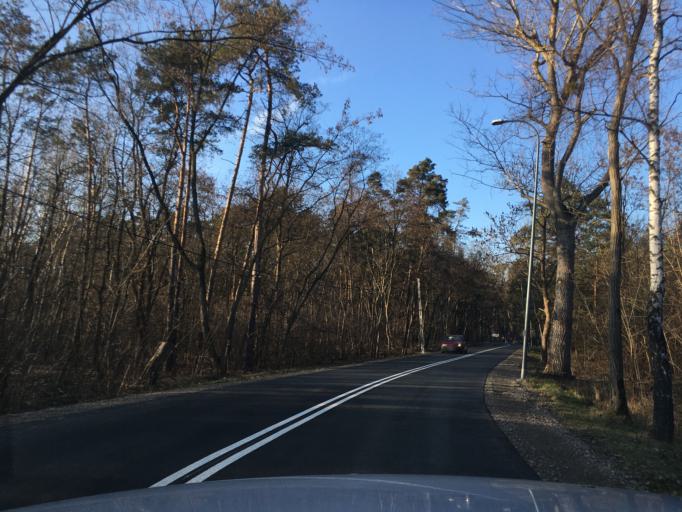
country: PL
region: Lodz Voivodeship
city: Zabia Wola
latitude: 52.0489
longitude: 20.7398
